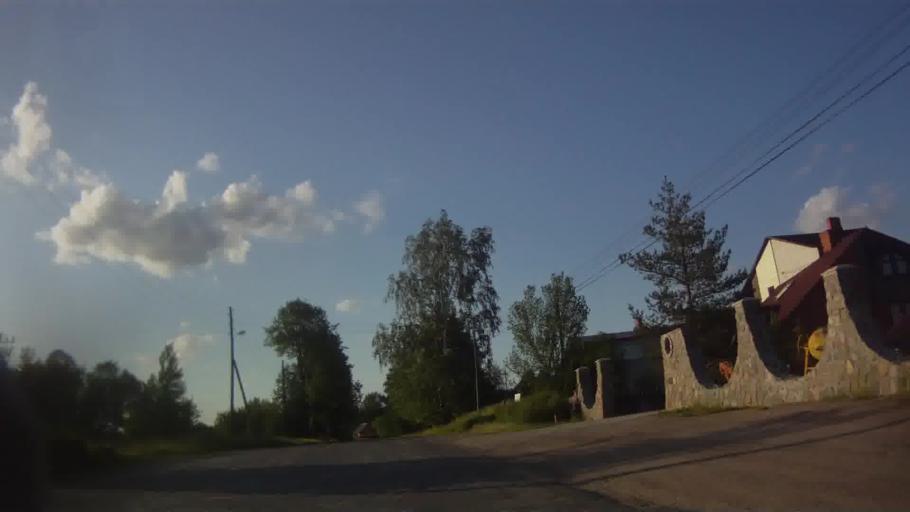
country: LV
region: Rezekne
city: Rezekne
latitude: 56.5254
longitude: 27.3184
